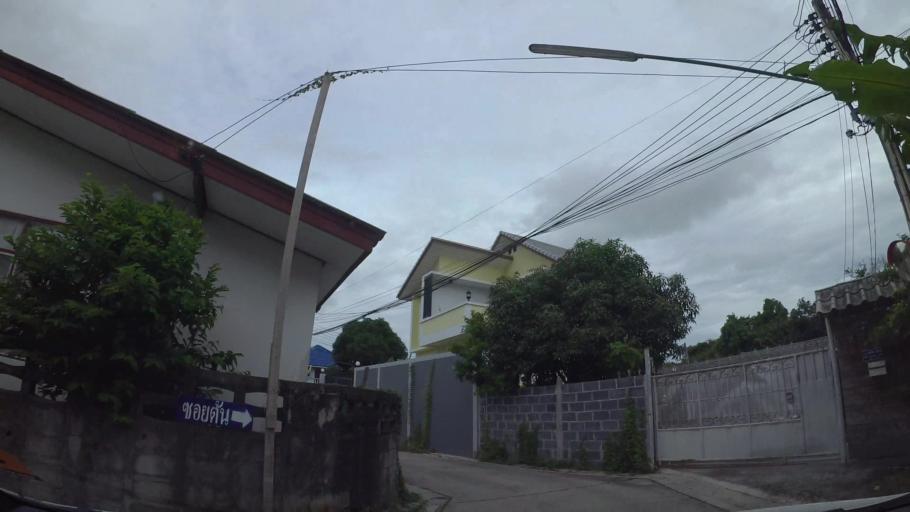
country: TH
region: Rayong
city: Rayong
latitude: 12.6757
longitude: 101.2669
